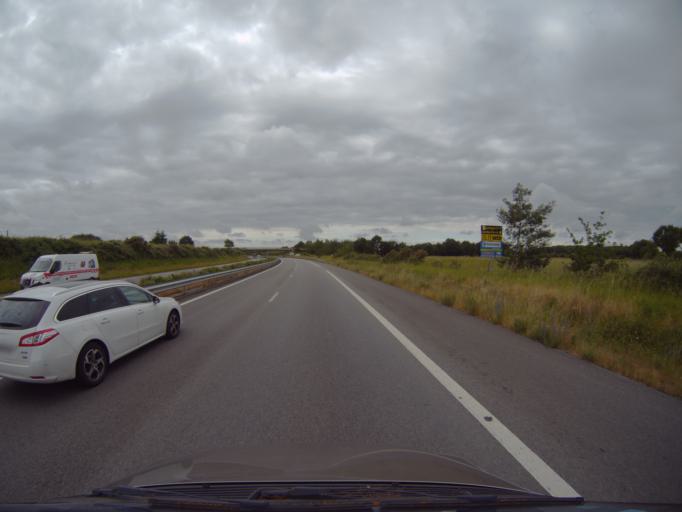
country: FR
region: Pays de la Loire
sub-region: Departement de la Loire-Atlantique
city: La Chevroliere
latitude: 47.0581
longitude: -1.6160
